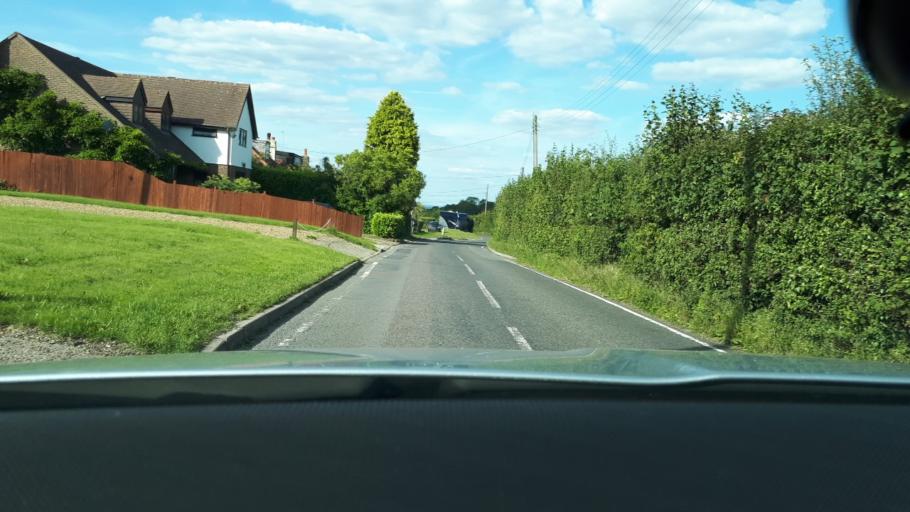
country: GB
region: England
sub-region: Kent
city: Biggin Hill
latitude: 51.3327
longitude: 0.0749
